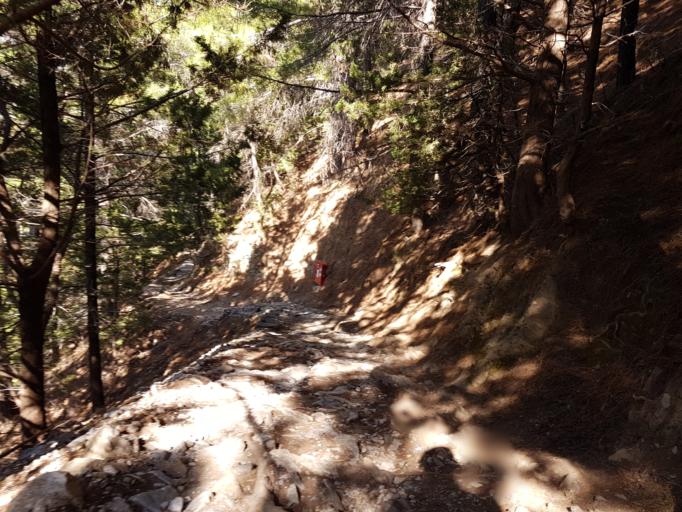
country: GR
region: Crete
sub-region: Nomos Chanias
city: Perivolia
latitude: 35.3086
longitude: 23.9256
